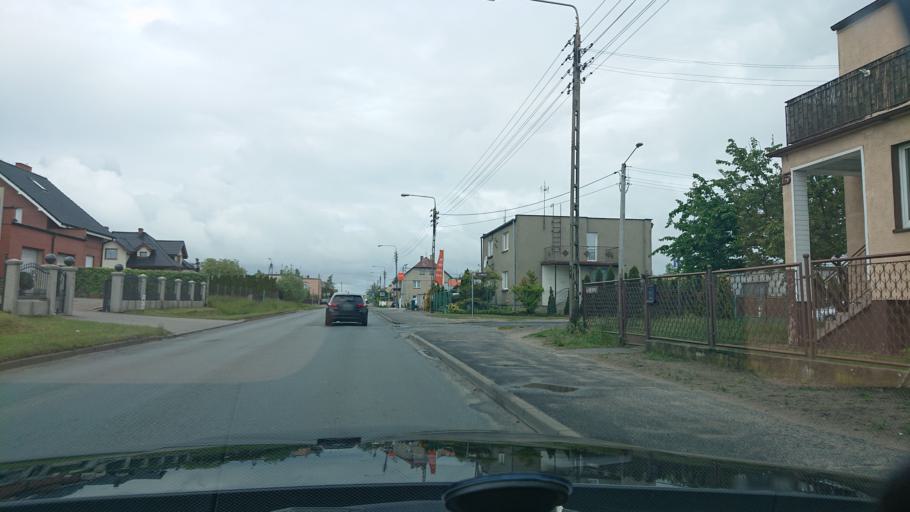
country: PL
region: Greater Poland Voivodeship
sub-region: Powiat gnieznienski
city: Gniezno
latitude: 52.5118
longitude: 17.6022
